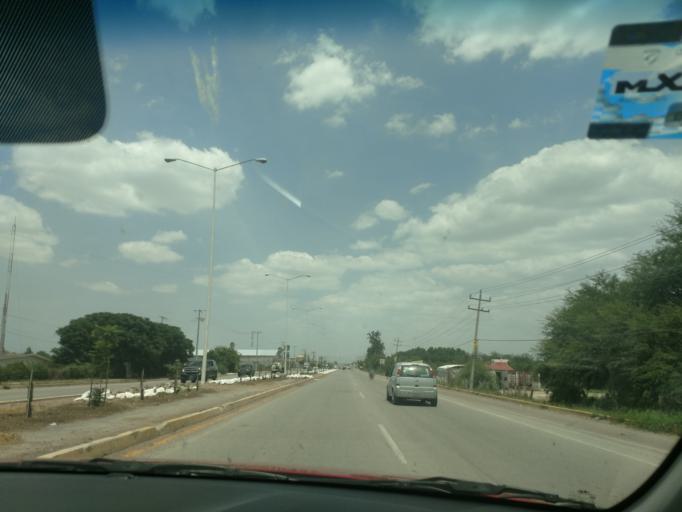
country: MX
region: San Luis Potosi
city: Ciudad Fernandez
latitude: 21.9383
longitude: -100.0333
